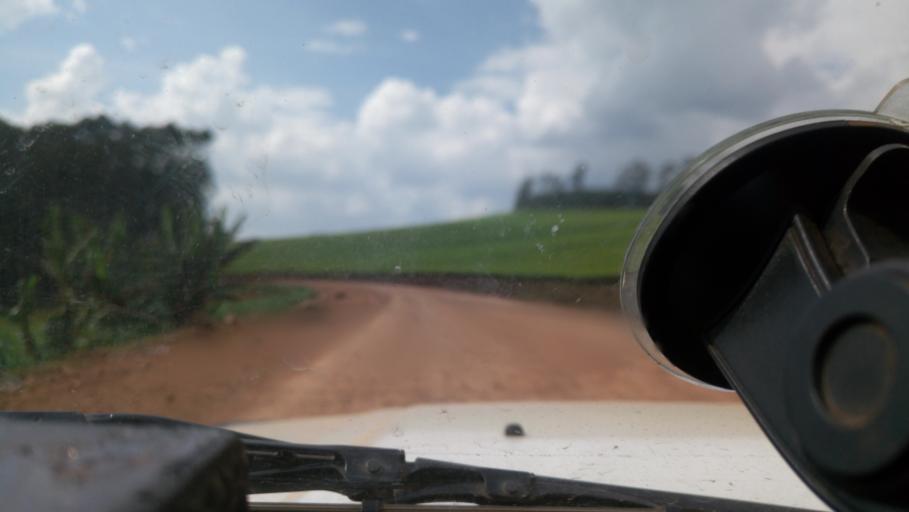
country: KE
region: Nyamira District
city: Nyamira
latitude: -0.5758
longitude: 35.0503
